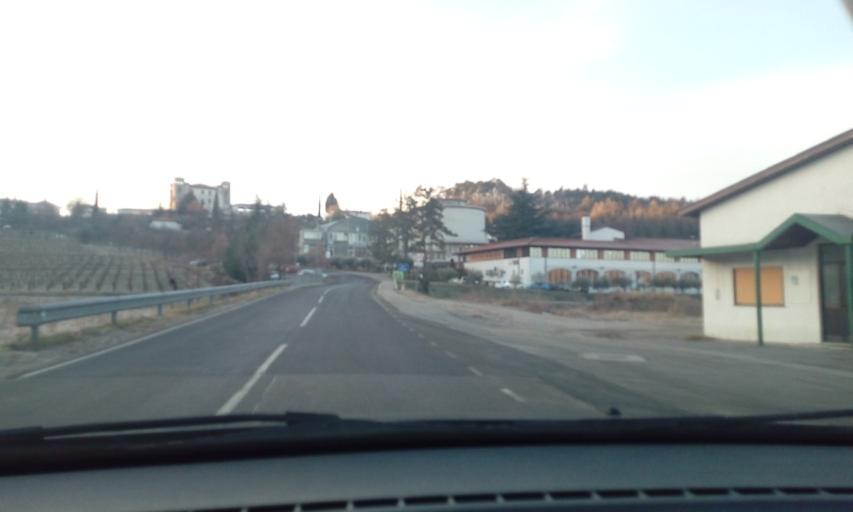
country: SI
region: Brda
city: Dobrovo
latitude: 46.0002
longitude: 13.5240
